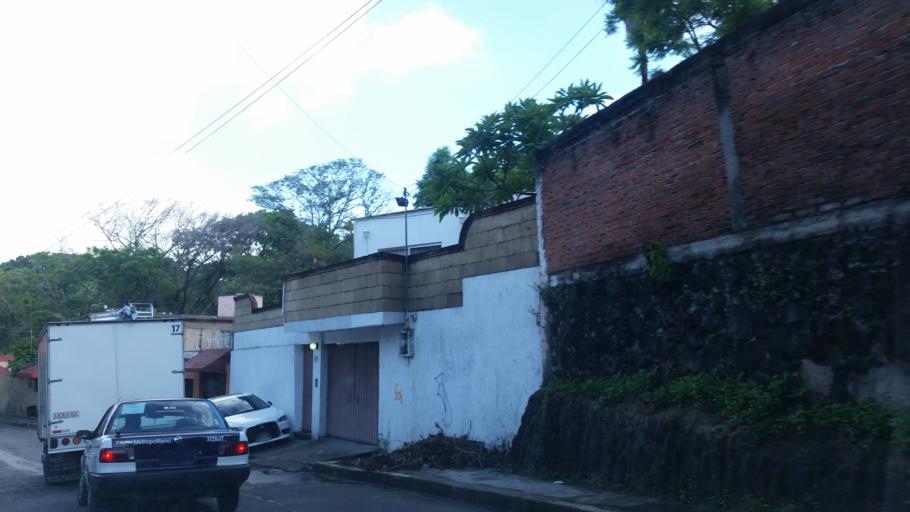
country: MX
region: Morelos
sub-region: Cuernavaca
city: Cuernavaca
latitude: 18.9198
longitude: -99.2084
